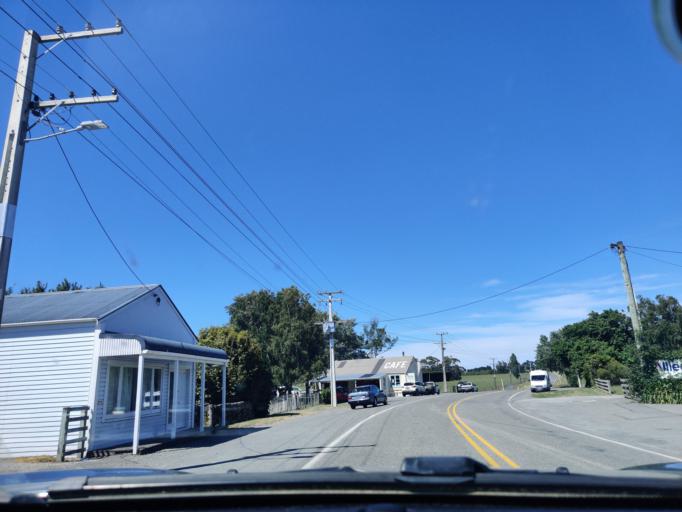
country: NZ
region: Wellington
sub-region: Upper Hutt City
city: Upper Hutt
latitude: -41.3523
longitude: 175.2057
